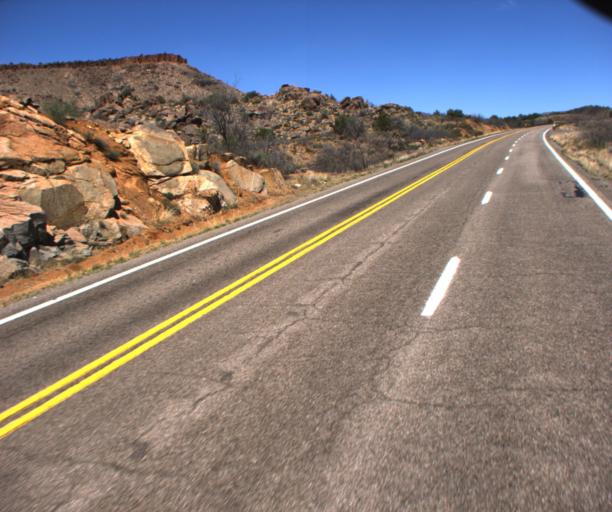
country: US
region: Arizona
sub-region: Mohave County
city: Peach Springs
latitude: 35.4291
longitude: -113.6493
